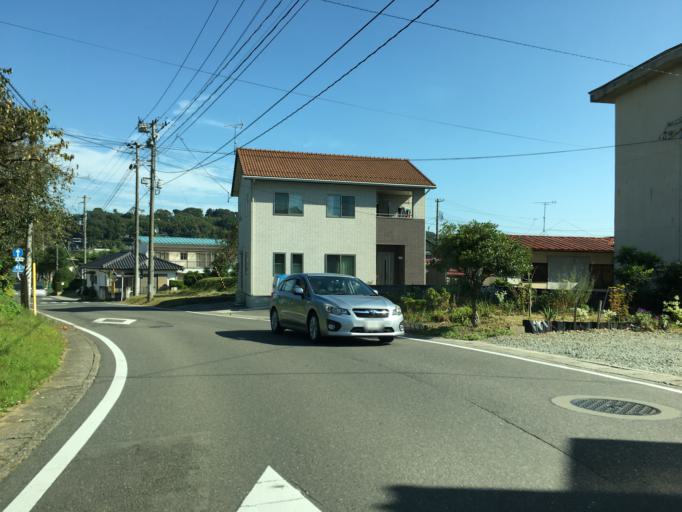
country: JP
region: Fukushima
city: Nihommatsu
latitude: 37.5870
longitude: 140.4267
